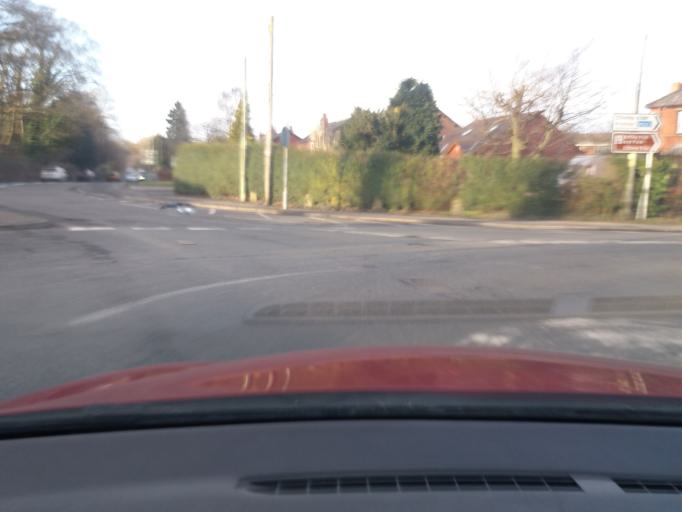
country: GB
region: England
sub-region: Lancashire
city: Euxton
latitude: 53.6610
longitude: -2.6747
